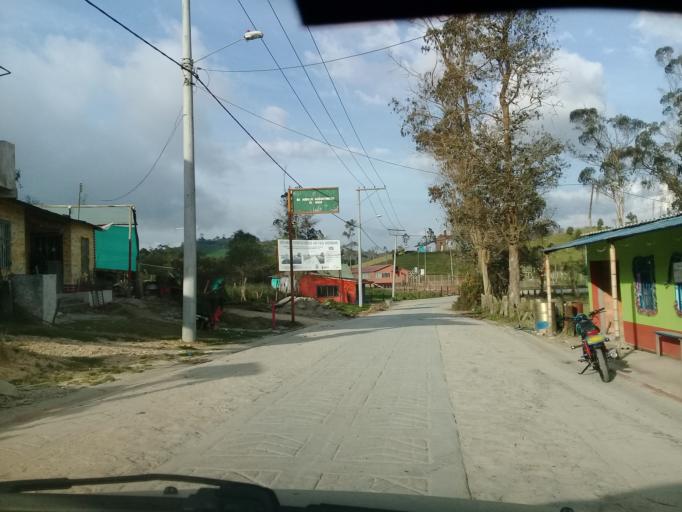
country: CO
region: Cundinamarca
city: Sibate
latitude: 4.4265
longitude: -74.2927
